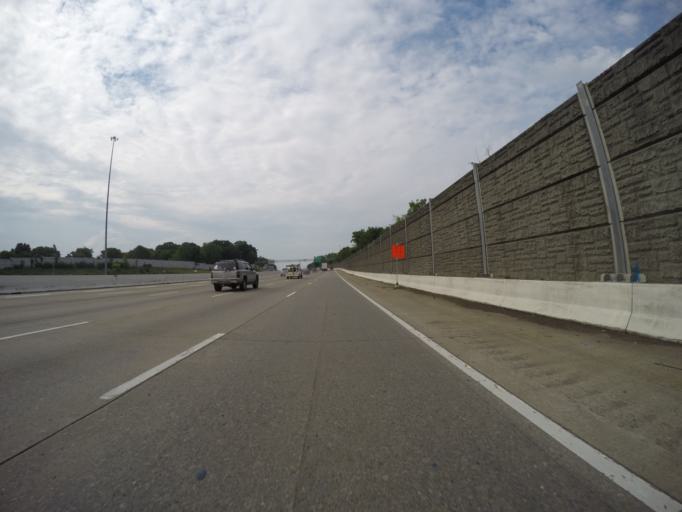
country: US
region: Tennessee
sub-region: Davidson County
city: Goodlettsville
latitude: 36.2637
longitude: -86.7380
